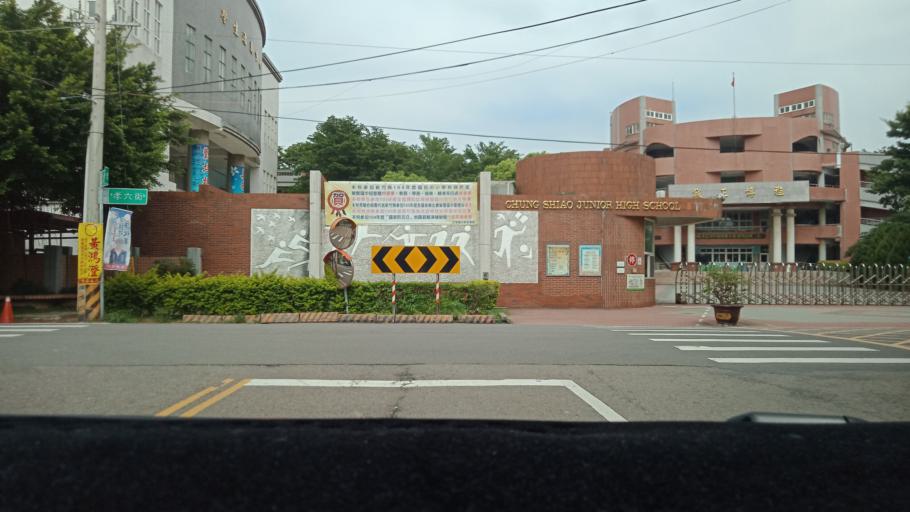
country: TW
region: Taiwan
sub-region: Hsinchu
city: Zhubei
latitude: 24.8790
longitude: 120.9994
